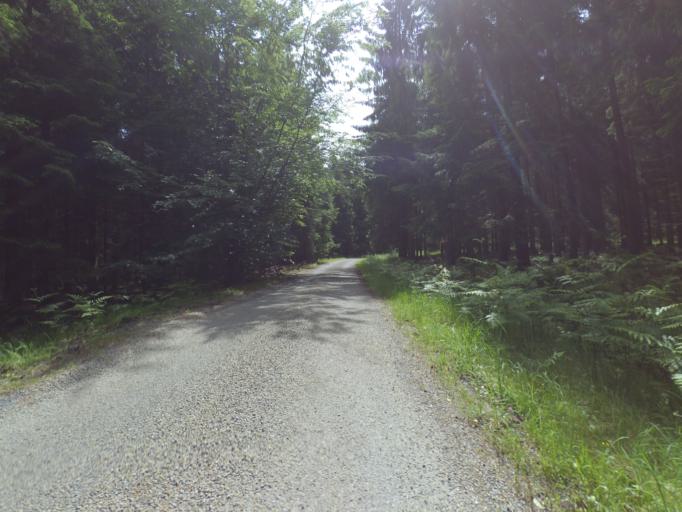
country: BE
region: Wallonia
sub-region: Province de Liege
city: Raeren
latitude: 50.5916
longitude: 6.1402
